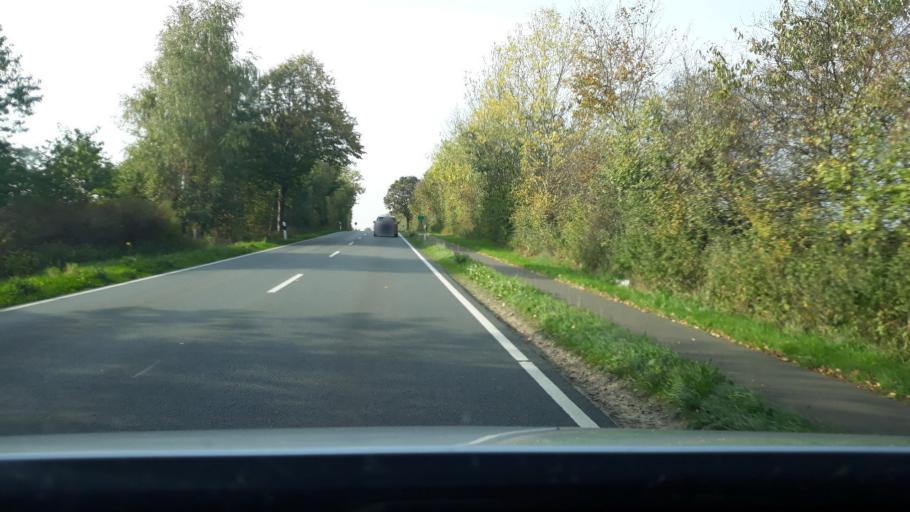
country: DE
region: Schleswig-Holstein
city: Owschlag
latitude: 54.4017
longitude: 9.6093
